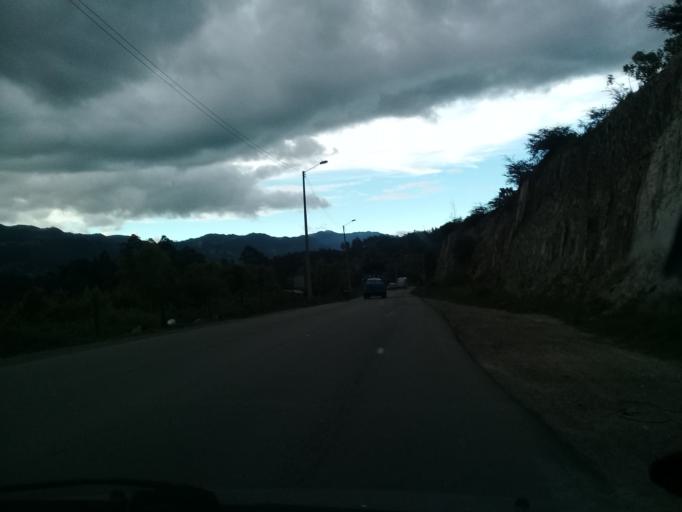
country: CO
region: Cundinamarca
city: Tabio
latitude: 4.9225
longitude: -74.0680
